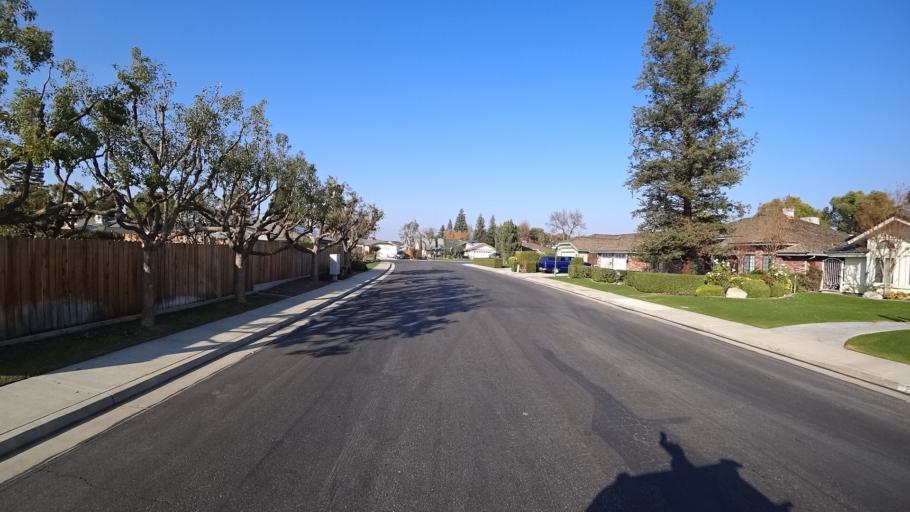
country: US
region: California
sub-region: Kern County
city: Greenacres
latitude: 35.3351
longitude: -119.1062
